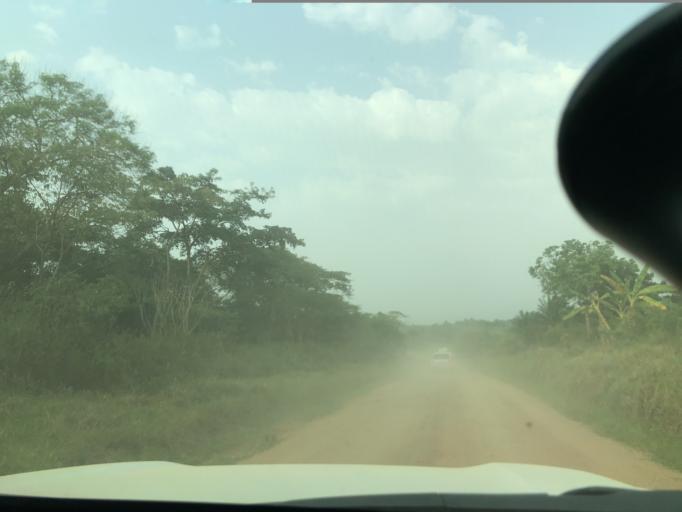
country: UG
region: Western Region
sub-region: Kasese District
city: Margherita
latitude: 0.2054
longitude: 29.6742
